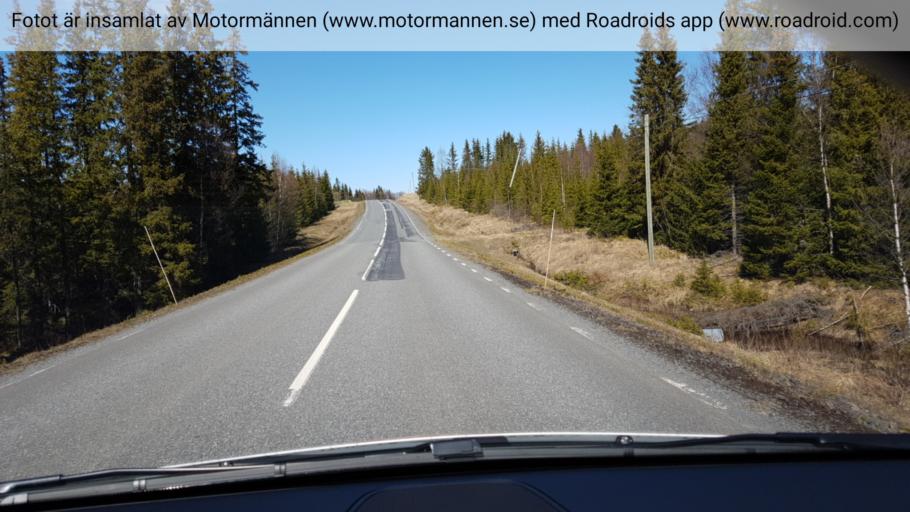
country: SE
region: Jaemtland
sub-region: Are Kommun
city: Are
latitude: 63.5781
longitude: 13.0205
